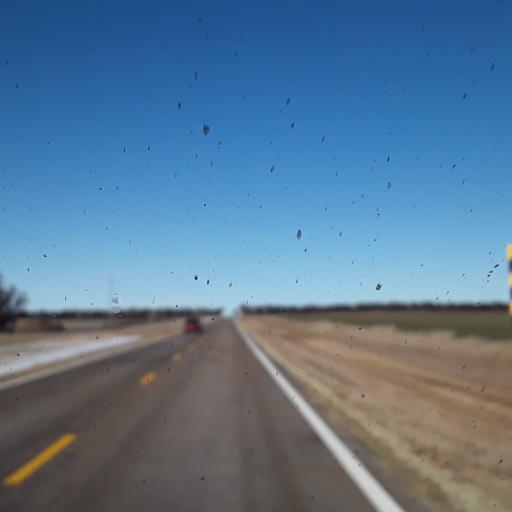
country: US
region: Kansas
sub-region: Mitchell County
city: Beloit
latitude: 39.3352
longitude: -98.1160
